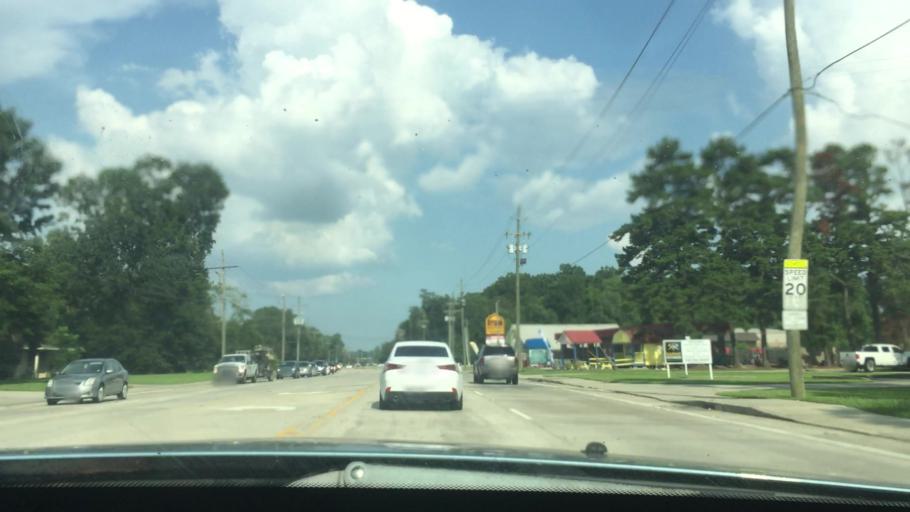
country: US
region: Louisiana
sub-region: East Baton Rouge Parish
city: Shenandoah
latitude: 30.4292
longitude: -91.0225
